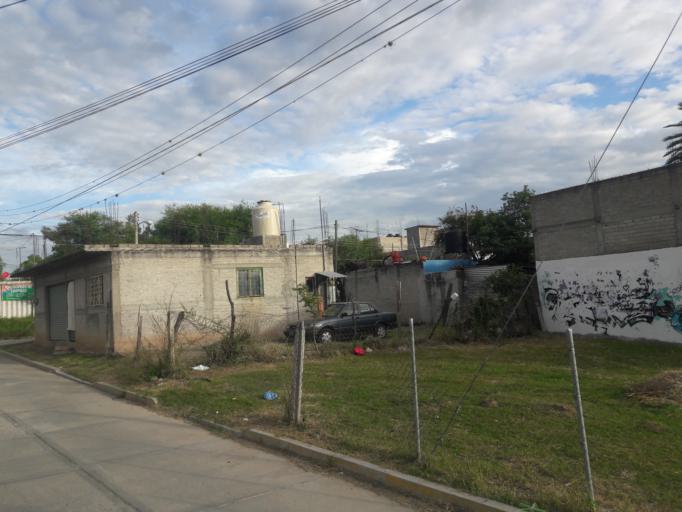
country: MX
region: Oaxaca
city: Ciudad de Huajuapam de Leon
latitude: 17.8027
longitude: -97.7858
